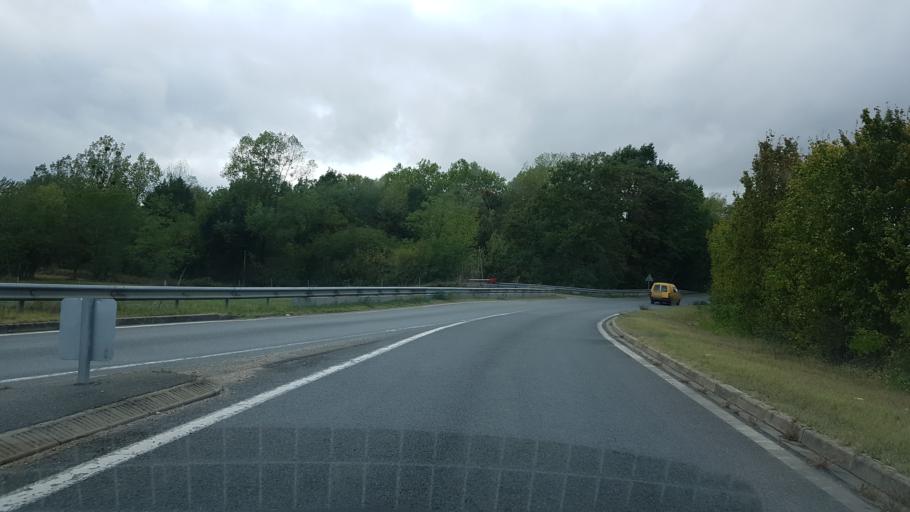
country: FR
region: Centre
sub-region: Departement du Loiret
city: Saint-Maurice-sur-Fessard
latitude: 47.9874
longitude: 2.6396
